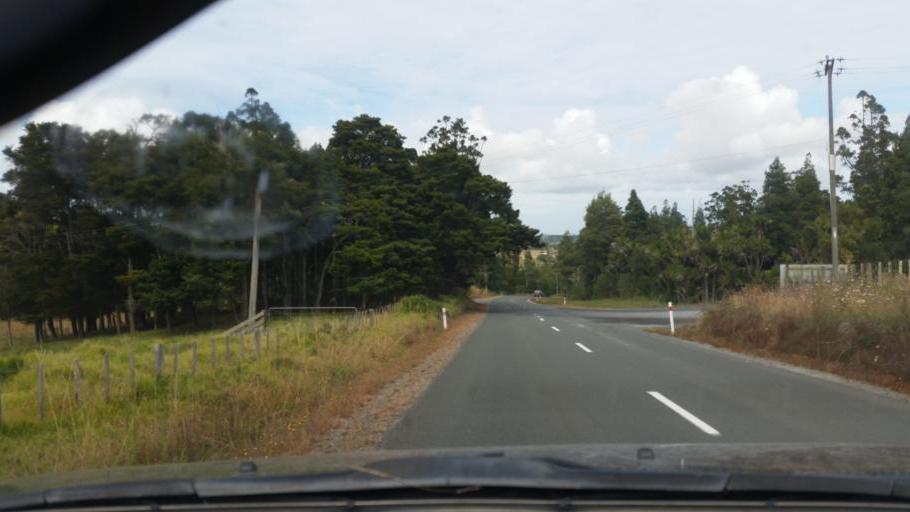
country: NZ
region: Northland
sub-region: Kaipara District
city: Dargaville
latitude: -35.9493
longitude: 173.9028
